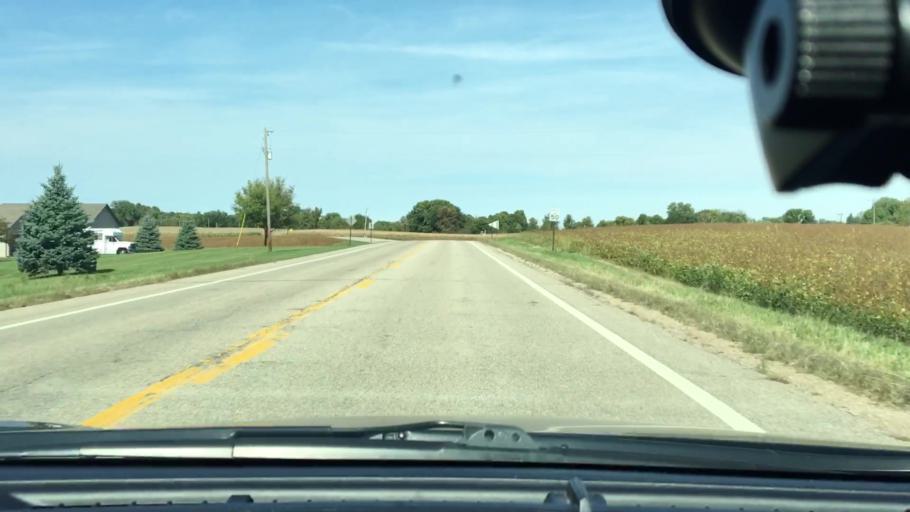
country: US
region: Minnesota
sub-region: Hennepin County
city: Corcoran
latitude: 45.1069
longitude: -93.5643
